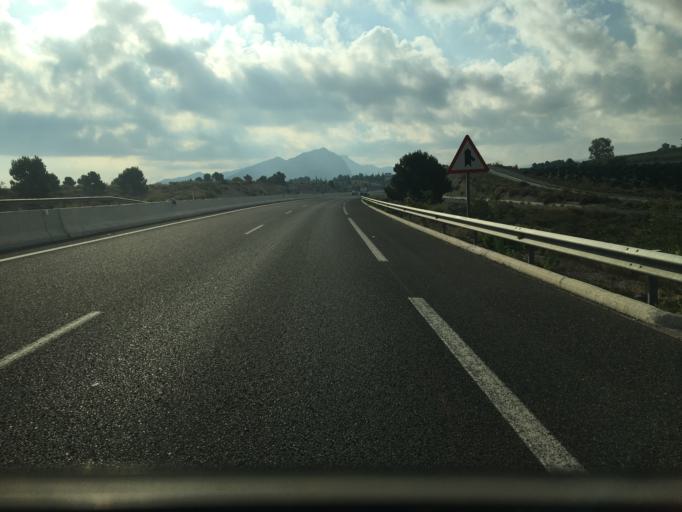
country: ES
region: Murcia
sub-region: Murcia
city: Beniel
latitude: 37.9967
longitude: -0.9847
